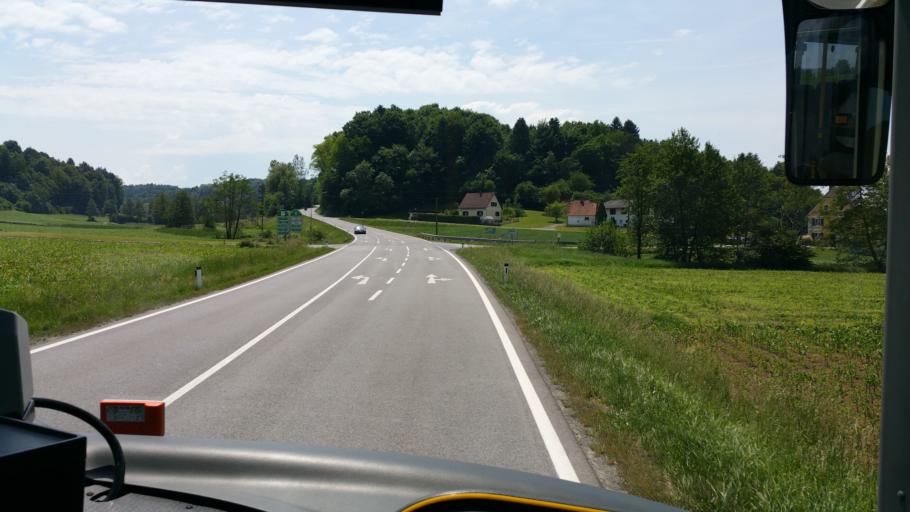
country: AT
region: Styria
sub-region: Politischer Bezirk Deutschlandsberg
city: Wettmannstatten
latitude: 46.8150
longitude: 15.3967
